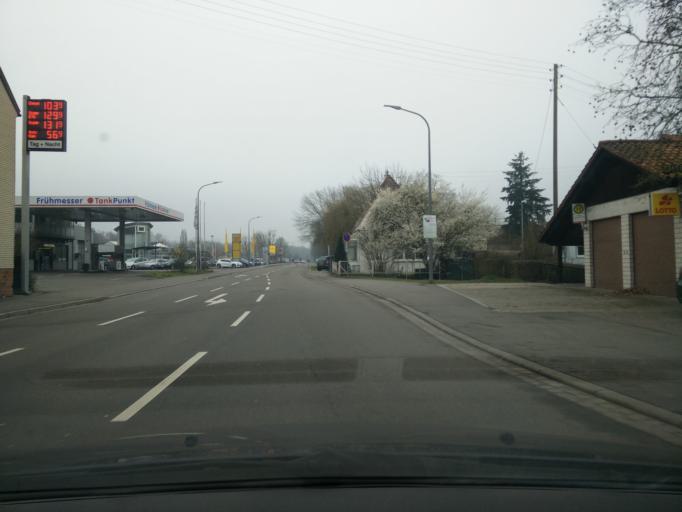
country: DE
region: Rheinland-Pfalz
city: Kandel
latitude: 49.0783
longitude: 8.2004
